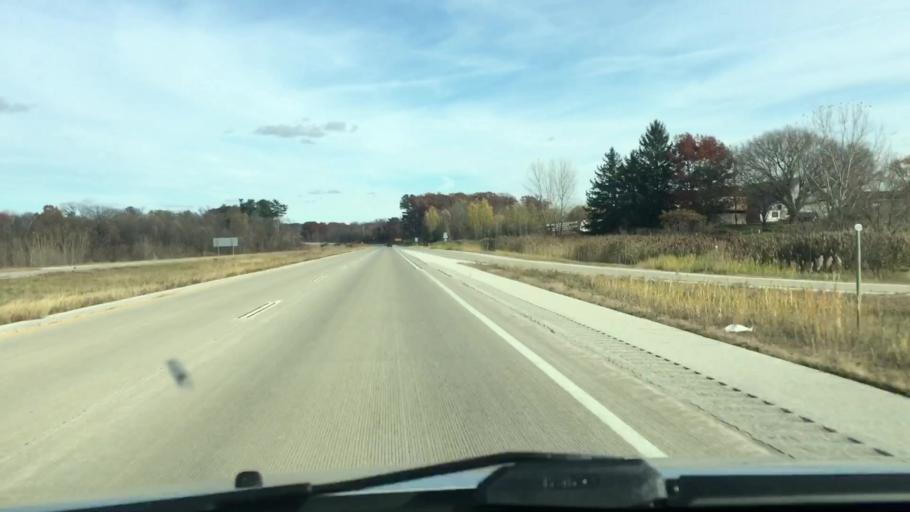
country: US
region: Wisconsin
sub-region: Kewaunee County
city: Luxemburg
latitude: 44.6337
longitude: -87.7721
